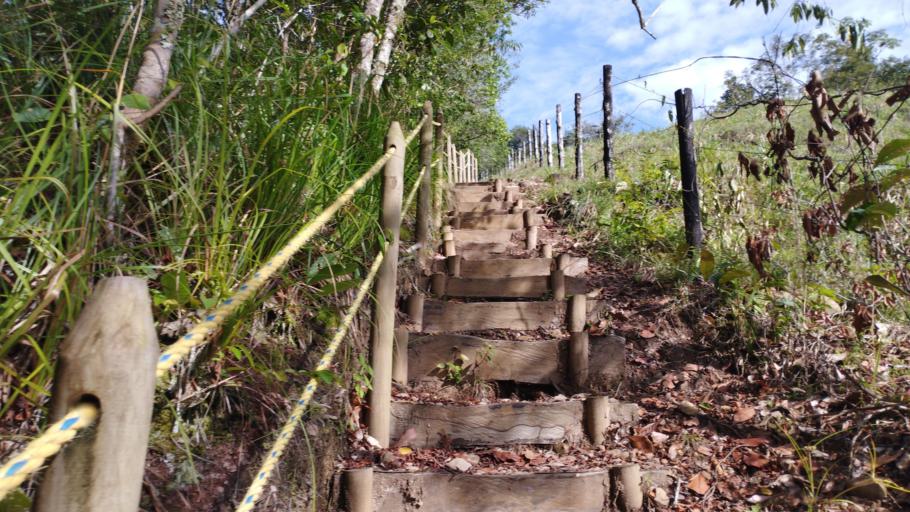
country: CO
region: Boyaca
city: San Luis de Gaceno
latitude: 4.8177
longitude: -73.1604
